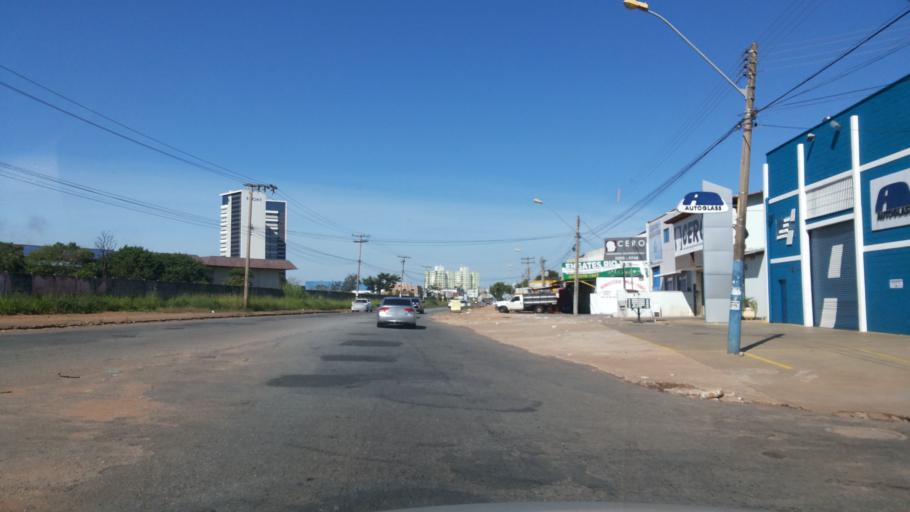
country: BR
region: Goias
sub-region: Goiania
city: Goiania
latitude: -16.7297
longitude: -49.2635
